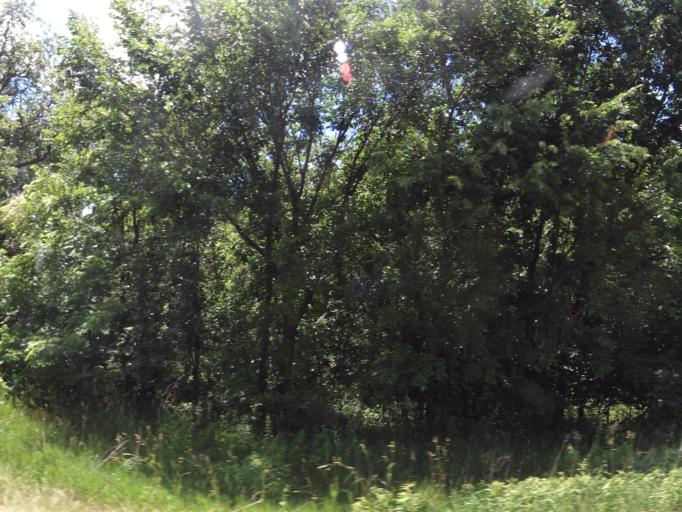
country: US
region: Iowa
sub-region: Buchanan County
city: Independence
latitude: 42.5005
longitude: -91.8896
